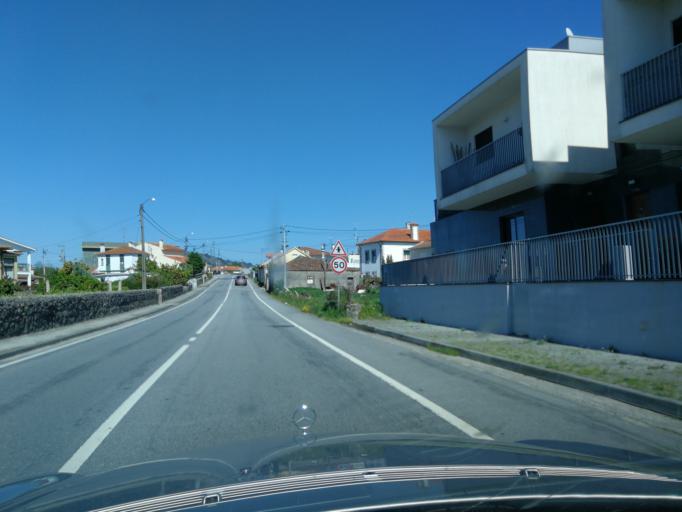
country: PT
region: Viana do Castelo
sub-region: Viana do Castelo
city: Meadela
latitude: 41.7059
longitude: -8.7885
